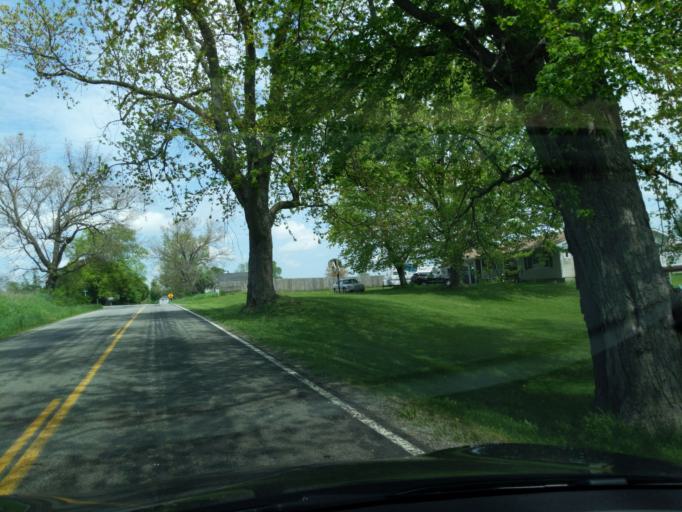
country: US
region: Michigan
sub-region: Ingham County
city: Stockbridge
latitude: 42.5075
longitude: -84.1600
